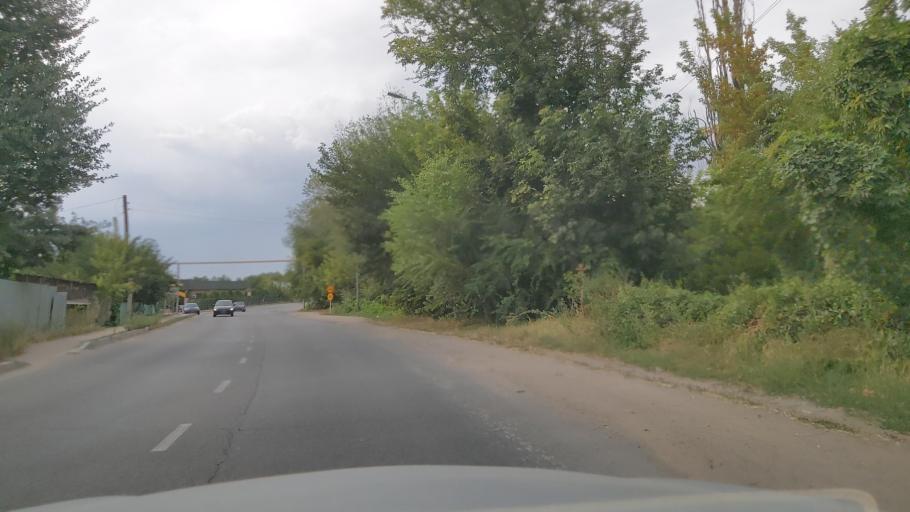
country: KZ
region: Almaty Oblysy
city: Energeticheskiy
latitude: 43.3880
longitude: 77.0766
